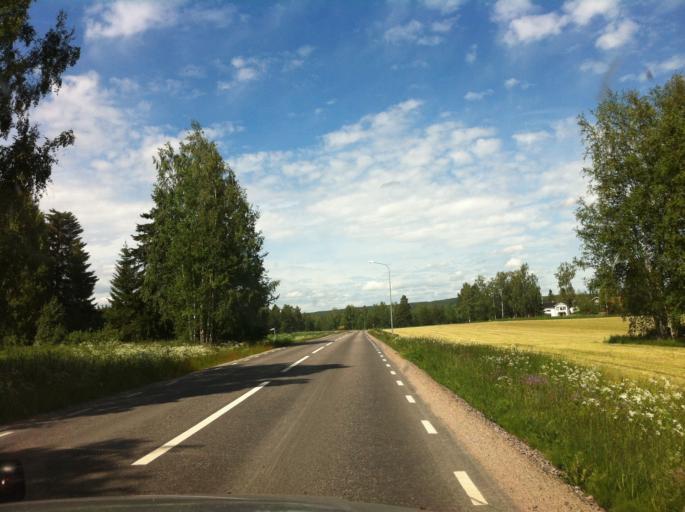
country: SE
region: Gaevleborg
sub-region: Ovanakers Kommun
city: Alfta
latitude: 61.3855
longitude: 16.0491
